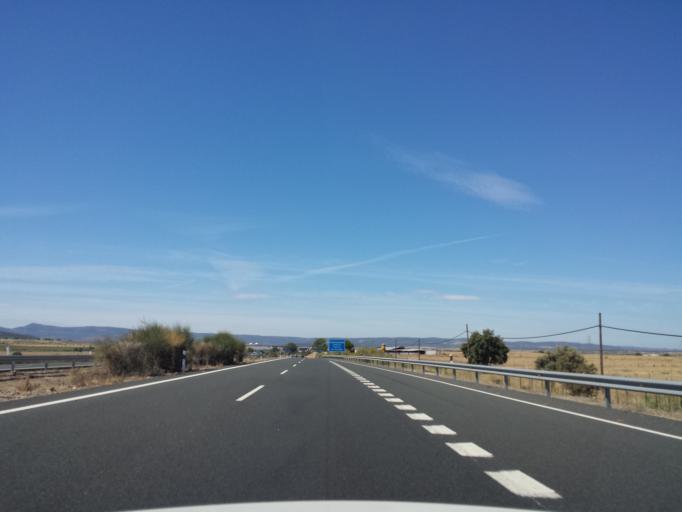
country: ES
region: Extremadura
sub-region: Provincia de Caceres
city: Saucedilla
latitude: 39.8488
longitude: -5.6321
